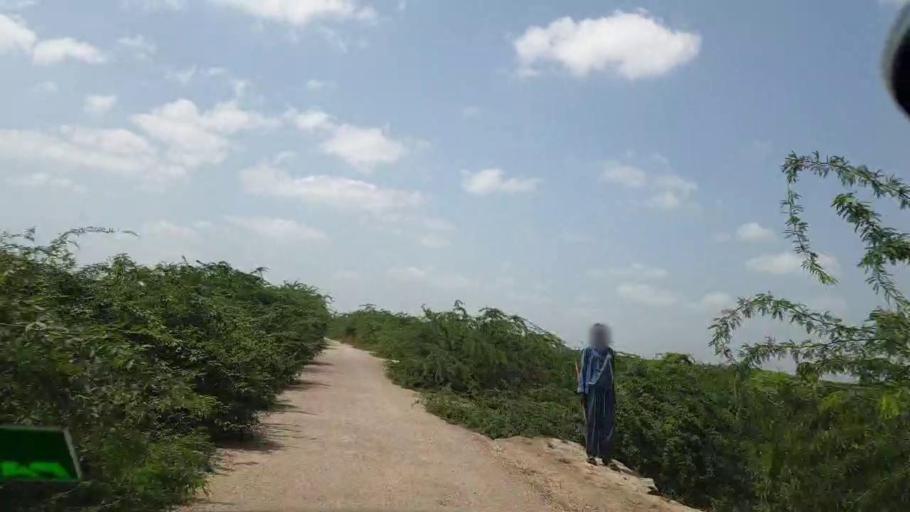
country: PK
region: Sindh
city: Kadhan
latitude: 24.5518
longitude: 69.1908
